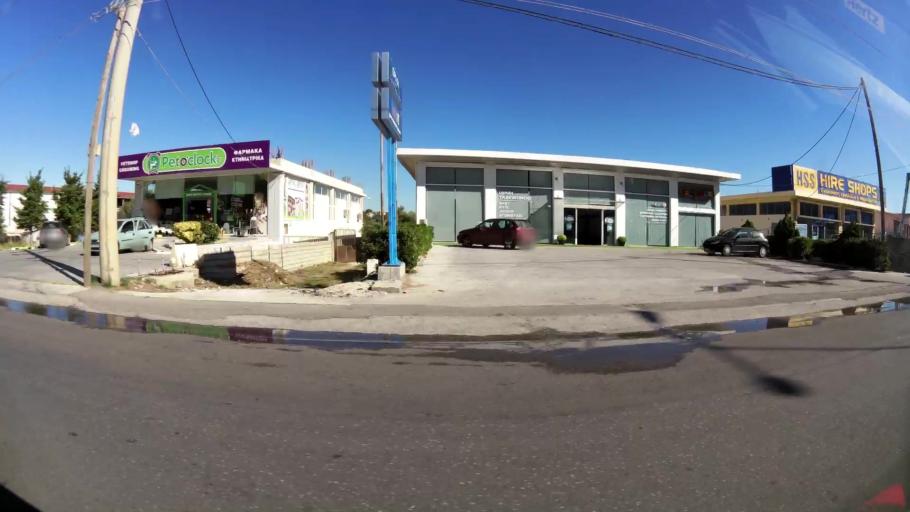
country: GR
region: Attica
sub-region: Nomarchia Anatolikis Attikis
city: Paiania
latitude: 37.9704
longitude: 23.8534
